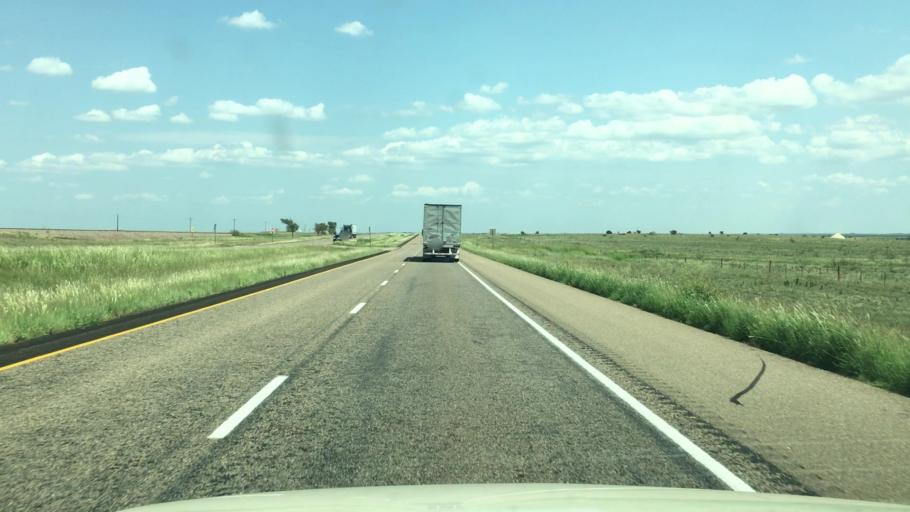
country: US
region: Texas
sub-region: Armstrong County
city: Claude
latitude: 35.0324
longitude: -101.1425
